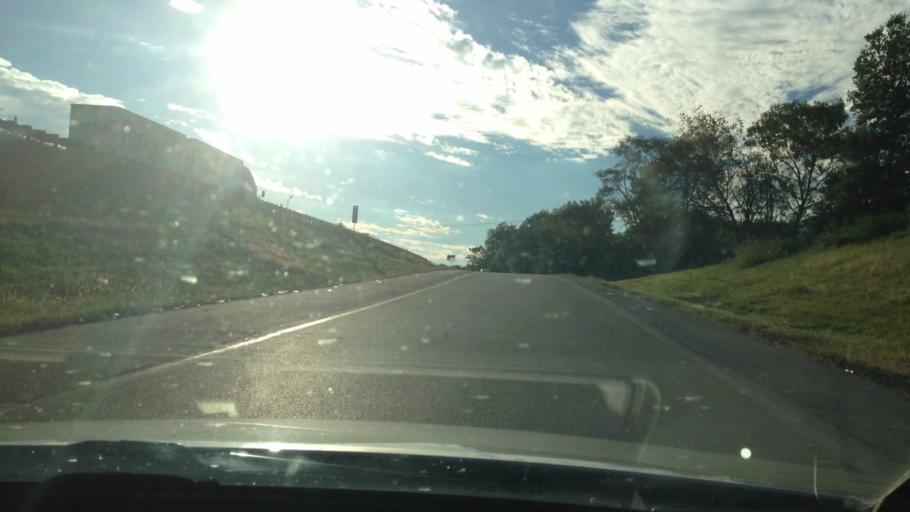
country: US
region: Missouri
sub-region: Clay County
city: Gladstone
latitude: 39.1723
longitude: -94.5516
